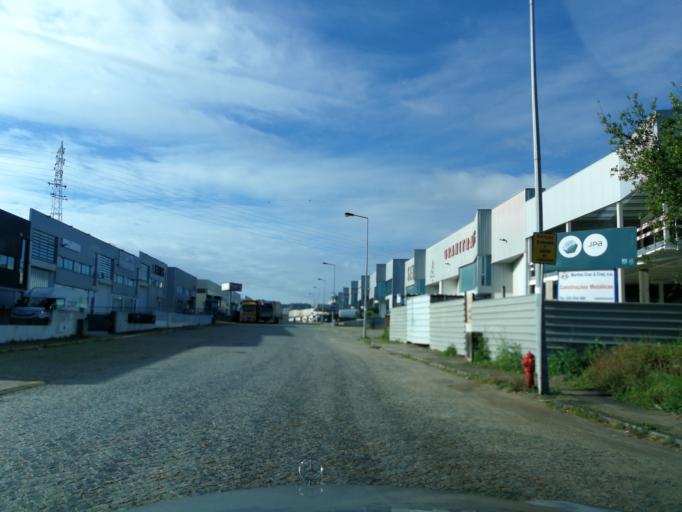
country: PT
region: Braga
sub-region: Braga
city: Braga
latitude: 41.5655
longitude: -8.4456
